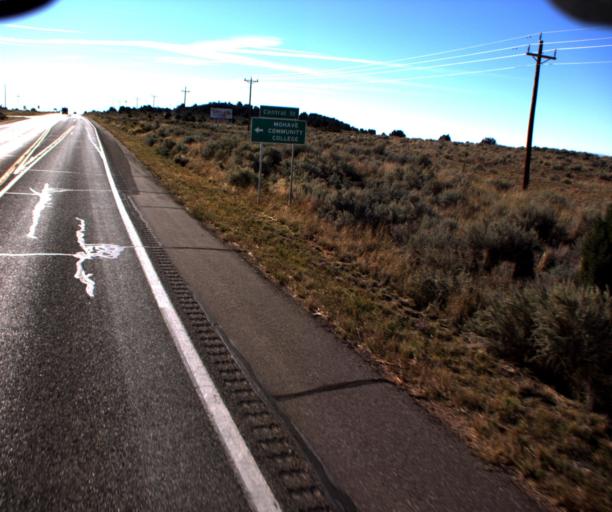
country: US
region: Arizona
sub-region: Mohave County
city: Colorado City
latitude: 36.9728
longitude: -112.9769
